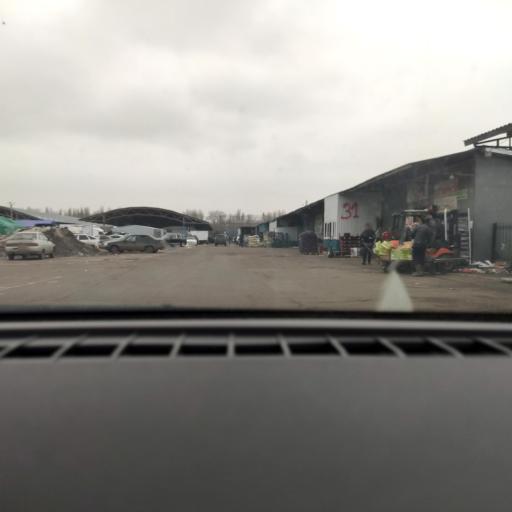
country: RU
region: Voronezj
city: Maslovka
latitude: 51.6125
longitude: 39.2616
